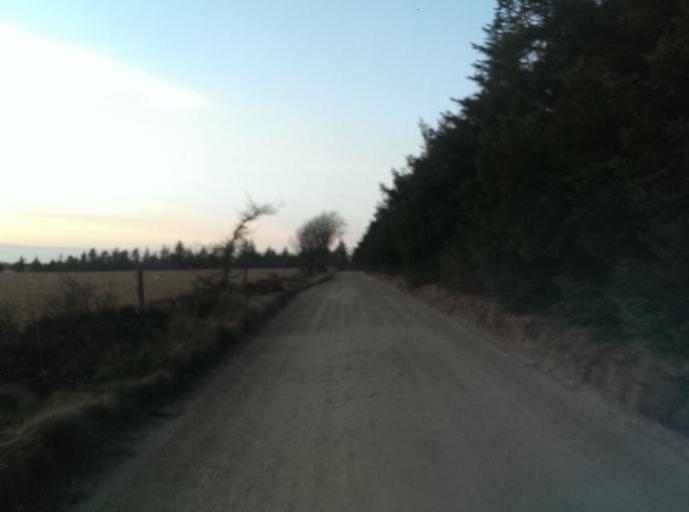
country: DK
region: South Denmark
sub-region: Varde Kommune
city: Oksbol
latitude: 55.5587
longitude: 8.3170
